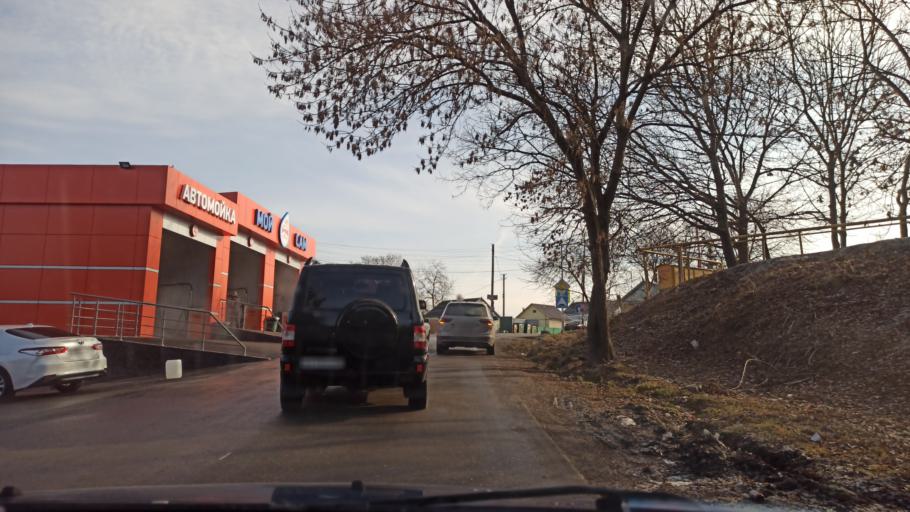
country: RU
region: Stavropol'skiy
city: Yessentuki
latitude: 44.0285
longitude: 42.8610
